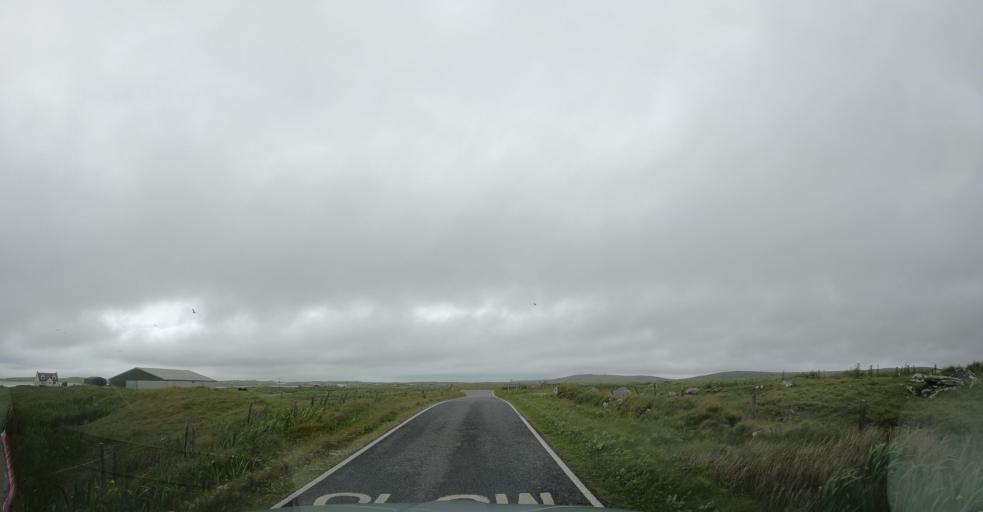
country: GB
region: Scotland
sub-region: Eilean Siar
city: Isle of North Uist
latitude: 57.5771
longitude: -7.4070
